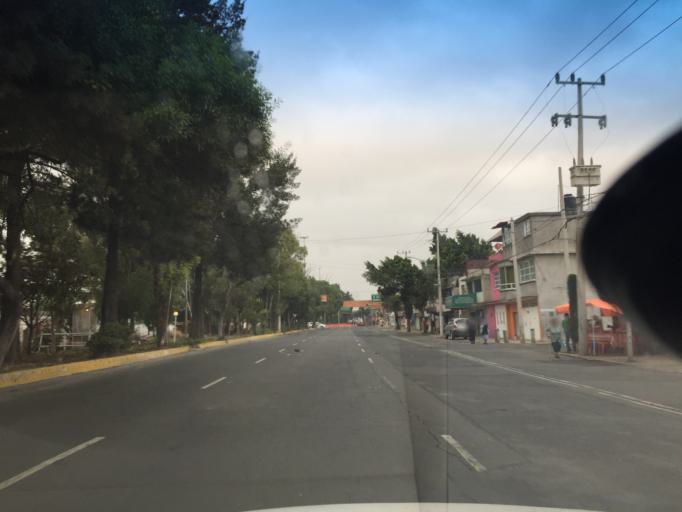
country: MX
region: Mexico City
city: Venustiano Carranza
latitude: 19.4670
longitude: -99.0786
